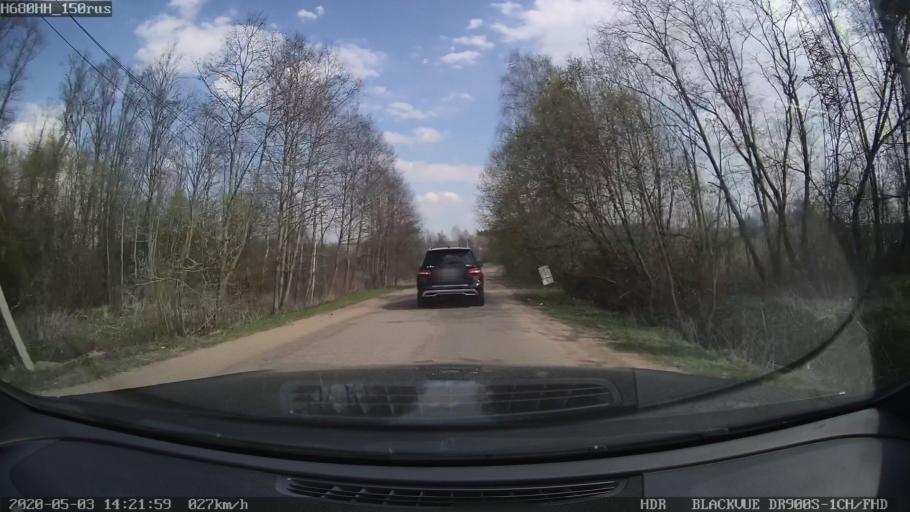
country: RU
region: Moskovskaya
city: Solnechnogorsk
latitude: 56.2576
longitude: 36.9839
